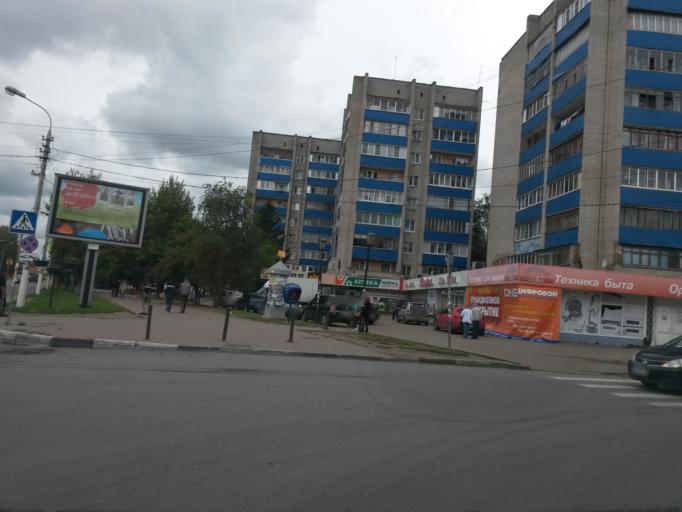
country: RU
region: Moskovskaya
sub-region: Chekhovskiy Rayon
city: Chekhov
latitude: 55.1485
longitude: 37.4881
